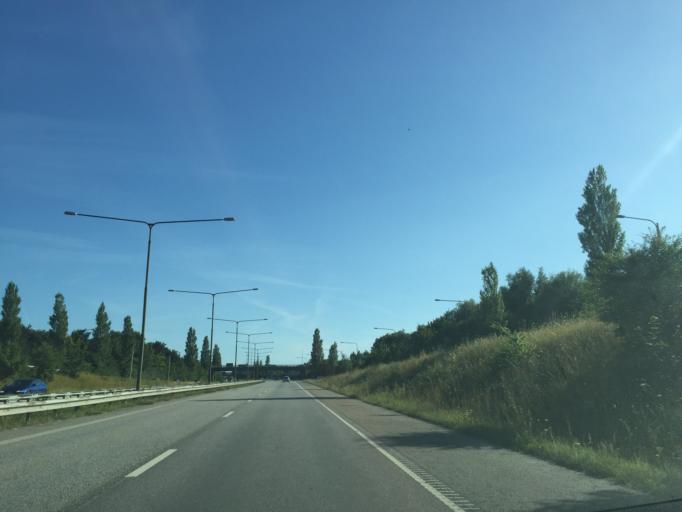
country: SE
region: Skane
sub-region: Malmo
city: Malmoe
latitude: 55.5631
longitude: 13.0009
